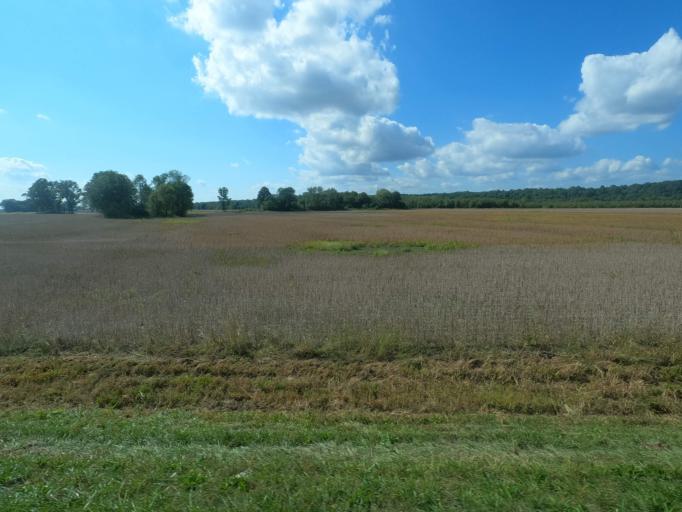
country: US
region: Illinois
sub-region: Massac County
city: Metropolis
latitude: 37.2940
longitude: -88.7562
